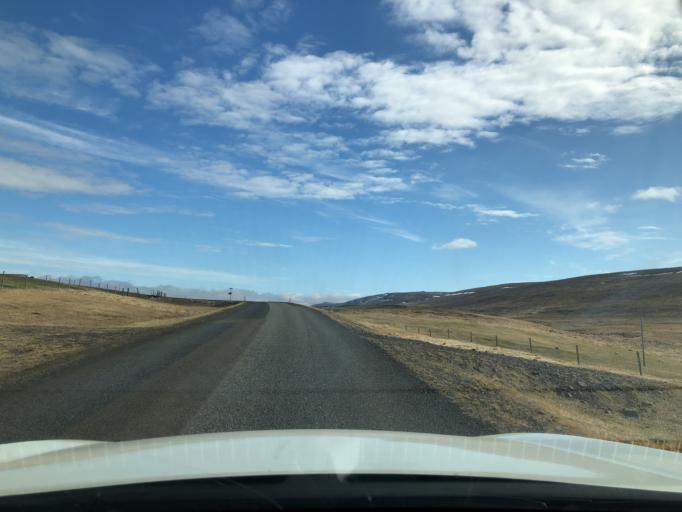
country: IS
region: West
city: Borgarnes
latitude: 65.1099
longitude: -21.6944
